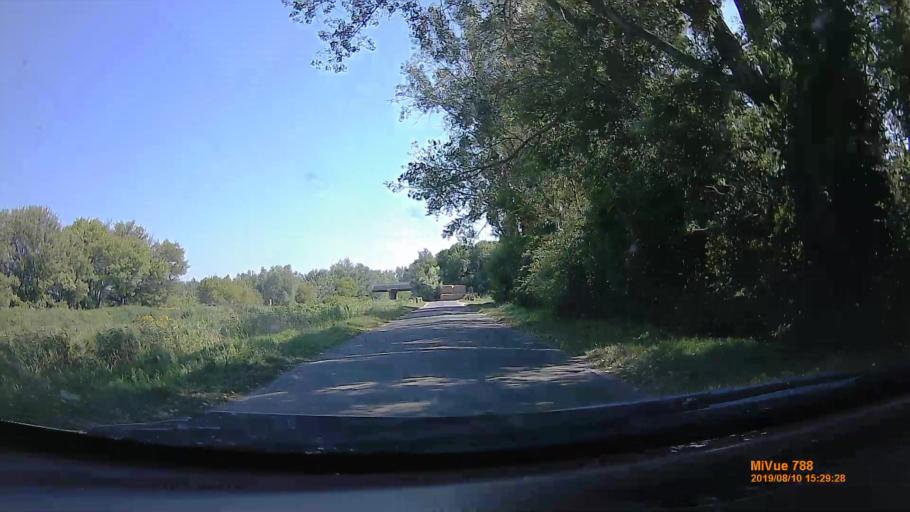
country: HU
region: Somogy
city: Balatonfenyves
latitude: 46.7049
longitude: 17.4823
